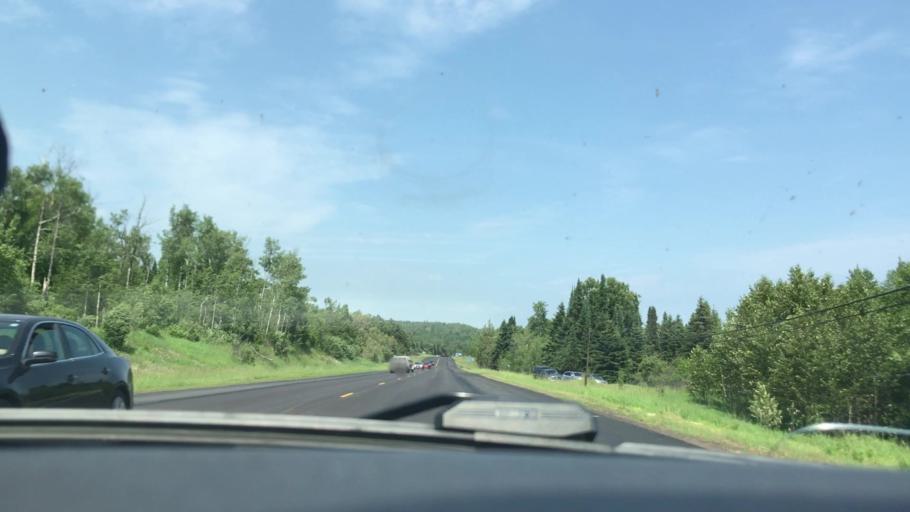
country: US
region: Minnesota
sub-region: Lake County
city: Silver Bay
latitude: 47.3291
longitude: -91.2092
